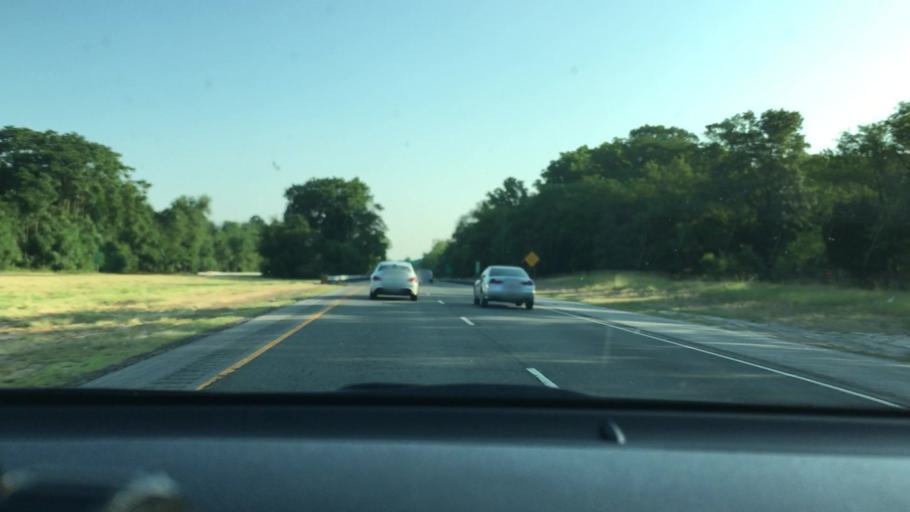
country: US
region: New Jersey
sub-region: Cumberland County
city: Vineland
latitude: 39.4803
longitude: -75.0723
